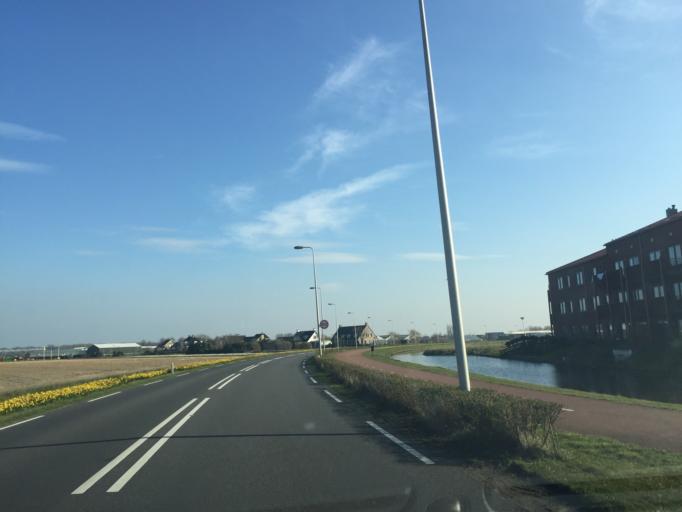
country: NL
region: South Holland
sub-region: Gemeente Noordwijkerhout
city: Noordwijkerhout
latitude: 52.2648
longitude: 4.5044
